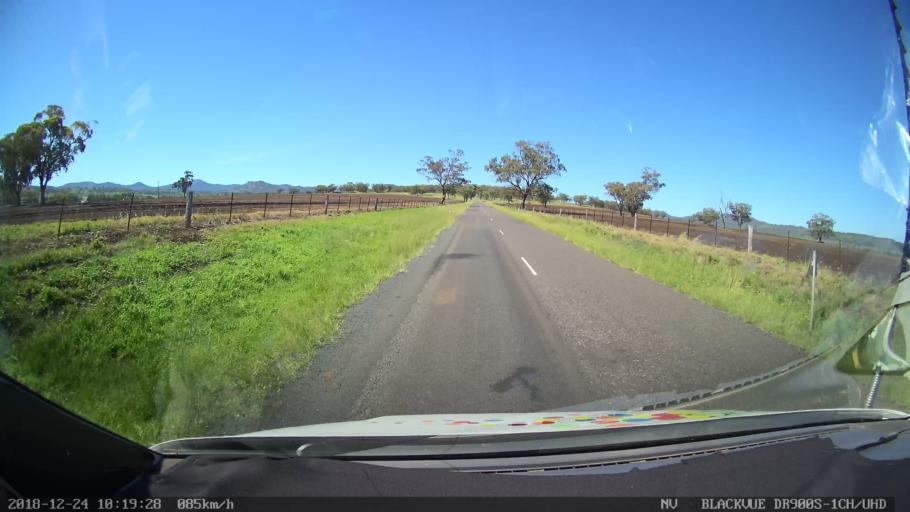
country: AU
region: New South Wales
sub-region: Liverpool Plains
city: Quirindi
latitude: -31.7309
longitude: 150.5651
